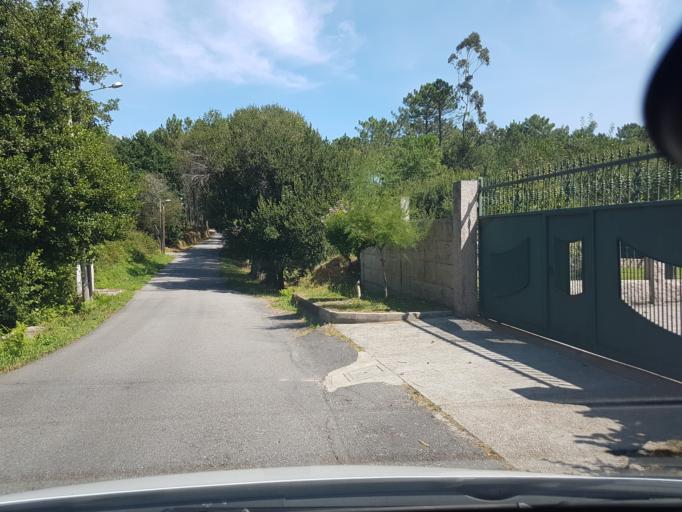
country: ES
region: Galicia
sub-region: Provincia de Pontevedra
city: Porrino
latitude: 42.2061
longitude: -8.6249
